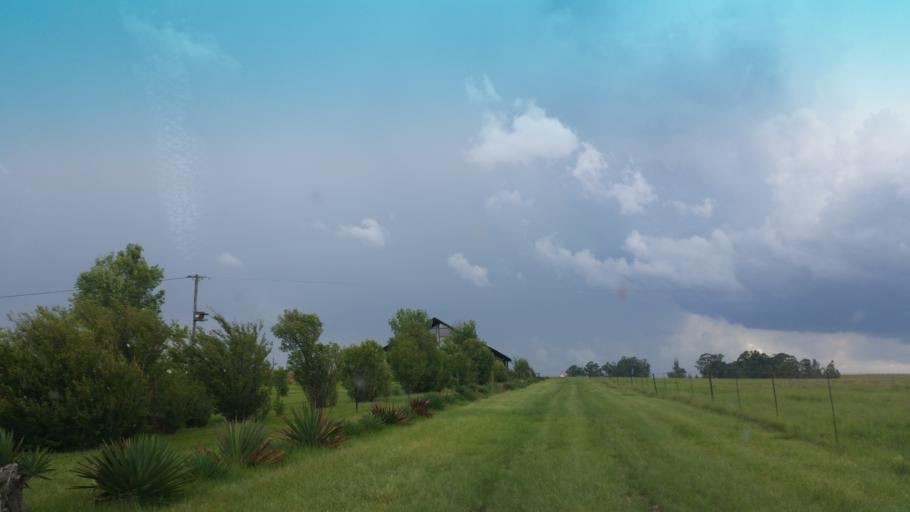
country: ZA
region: Orange Free State
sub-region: Thabo Mofutsanyana District Municipality
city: Harrismith
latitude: -28.1917
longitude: 29.0132
